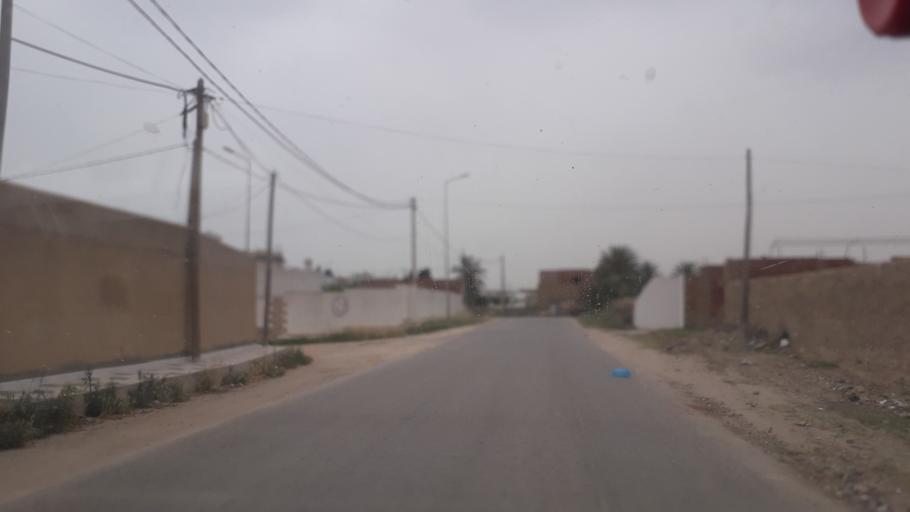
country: TN
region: Safaqis
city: Al Qarmadah
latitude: 34.7932
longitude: 10.7642
